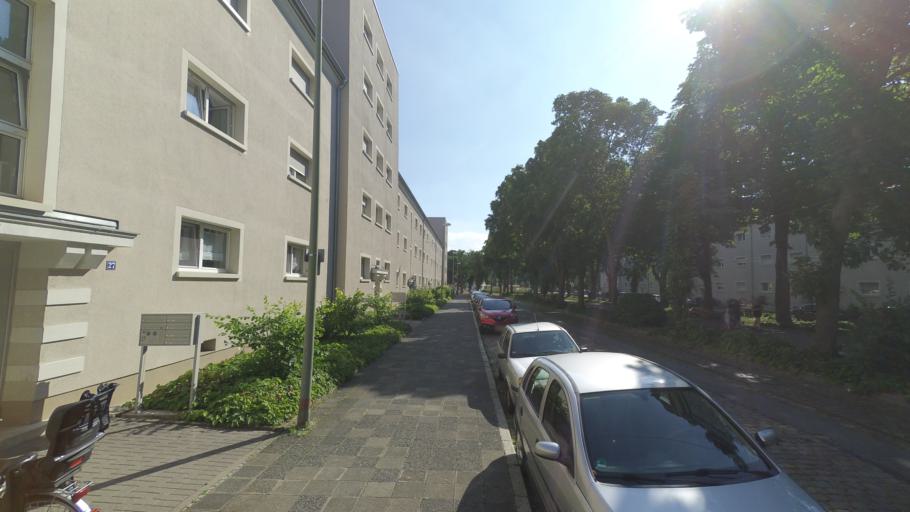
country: DE
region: Rheinland-Pfalz
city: Ludwigshafen am Rhein
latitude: 49.4911
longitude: 8.4196
